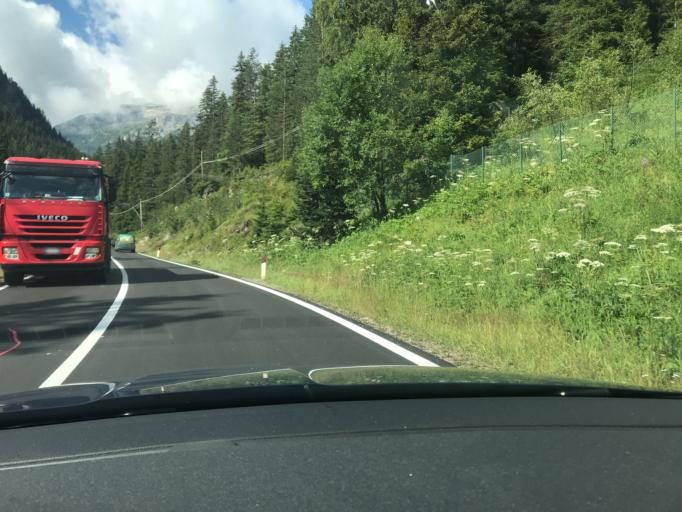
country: IT
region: Trentino-Alto Adige
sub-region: Bolzano
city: Corvara in Badia
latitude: 46.5619
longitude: 11.8832
